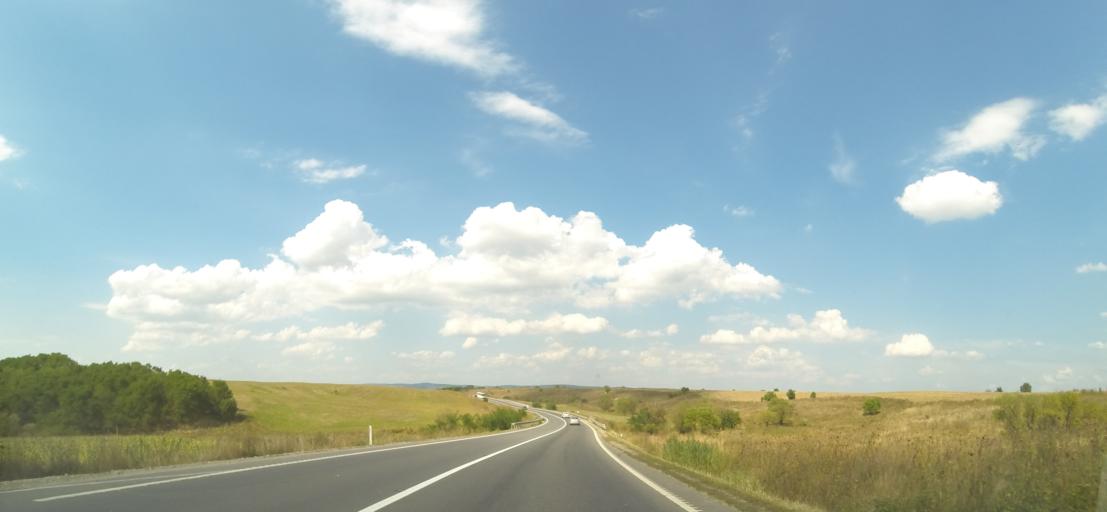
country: RO
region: Brasov
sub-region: Comuna Sercaia
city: Sercaia
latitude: 45.8116
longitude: 25.1674
